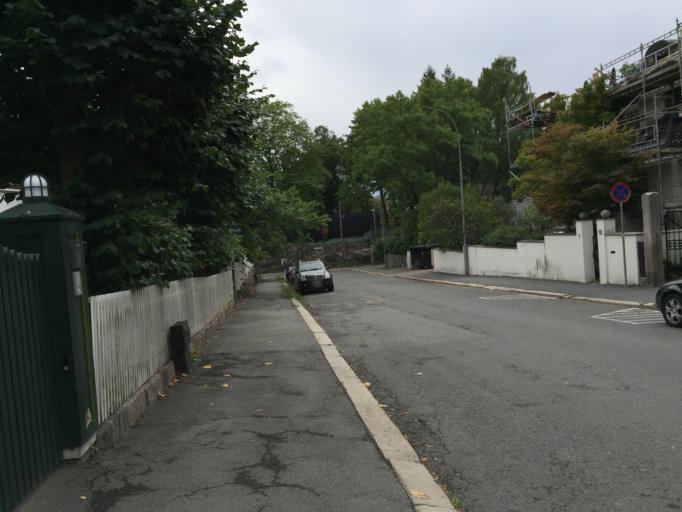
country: NO
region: Oslo
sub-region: Oslo
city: Sjolyststranda
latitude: 59.9158
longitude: 10.7040
